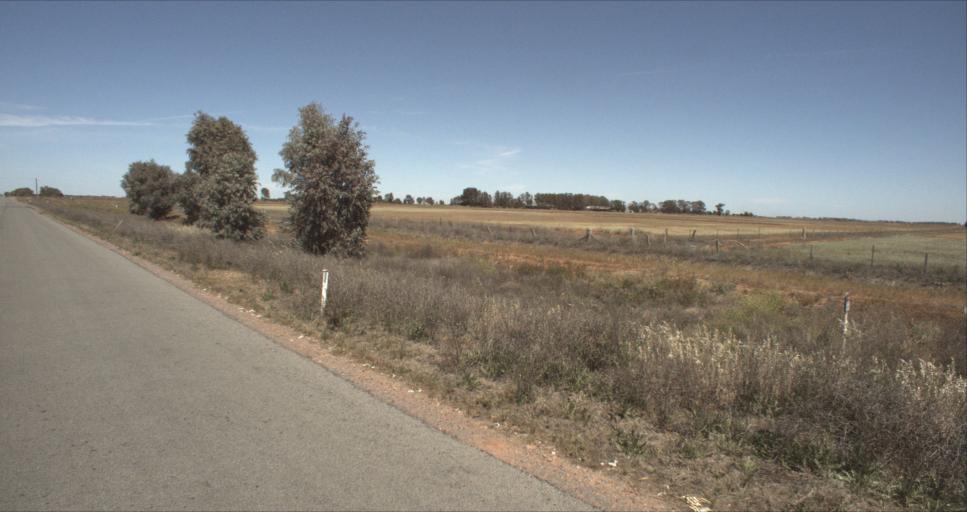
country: AU
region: New South Wales
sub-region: Leeton
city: Leeton
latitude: -34.4367
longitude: 146.2986
